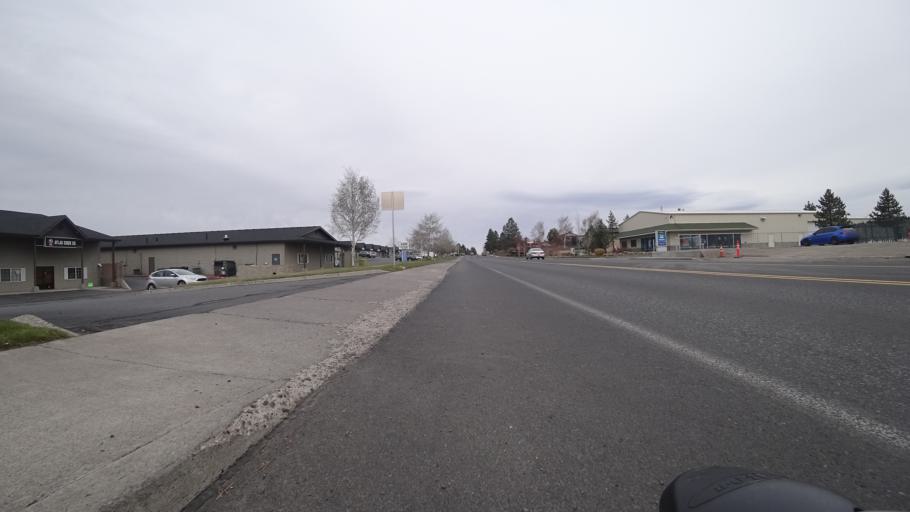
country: US
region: Oregon
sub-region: Deschutes County
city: Bend
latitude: 44.0443
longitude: -121.2922
